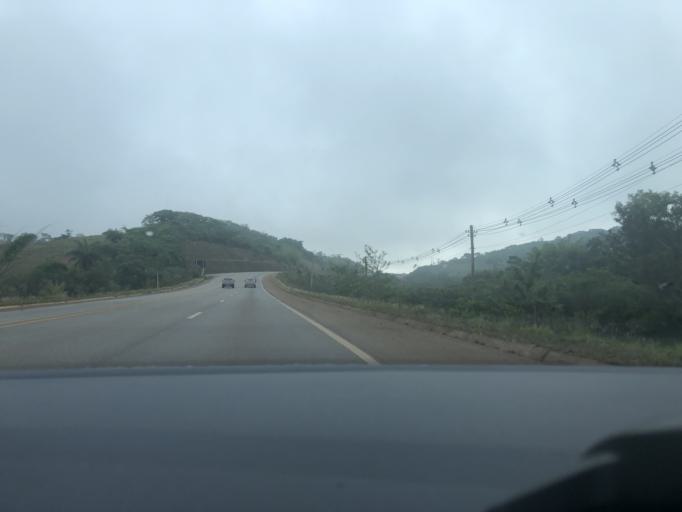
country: BR
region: Minas Gerais
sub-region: Congonhas
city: Congonhas
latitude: -20.5976
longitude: -43.9378
